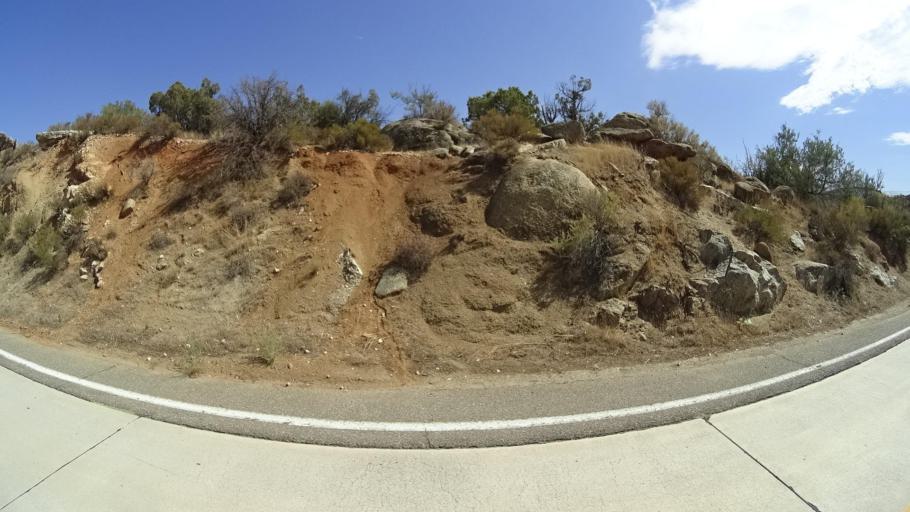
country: MX
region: Baja California
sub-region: Tecate
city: Cereso del Hongo
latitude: 32.6144
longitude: -116.1952
